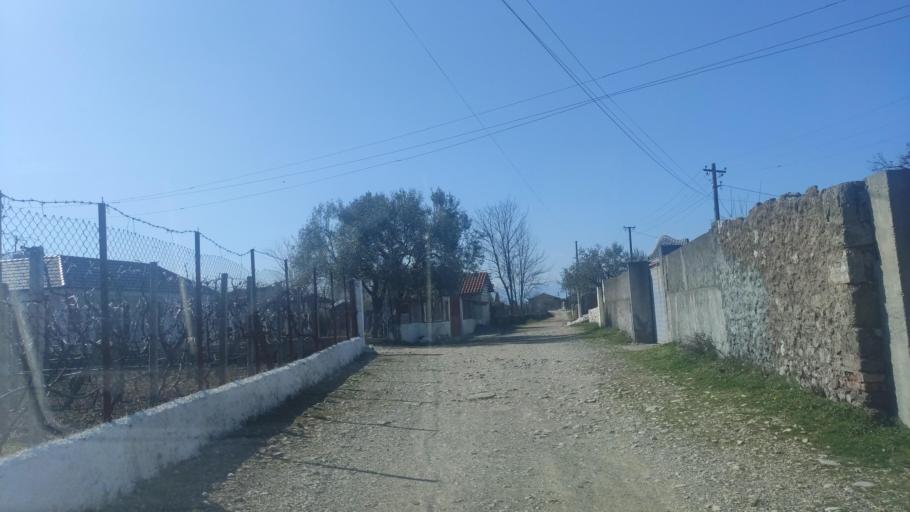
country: AL
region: Shkoder
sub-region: Rrethi i Malesia e Madhe
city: Grude-Fushe
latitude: 42.1714
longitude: 19.4845
